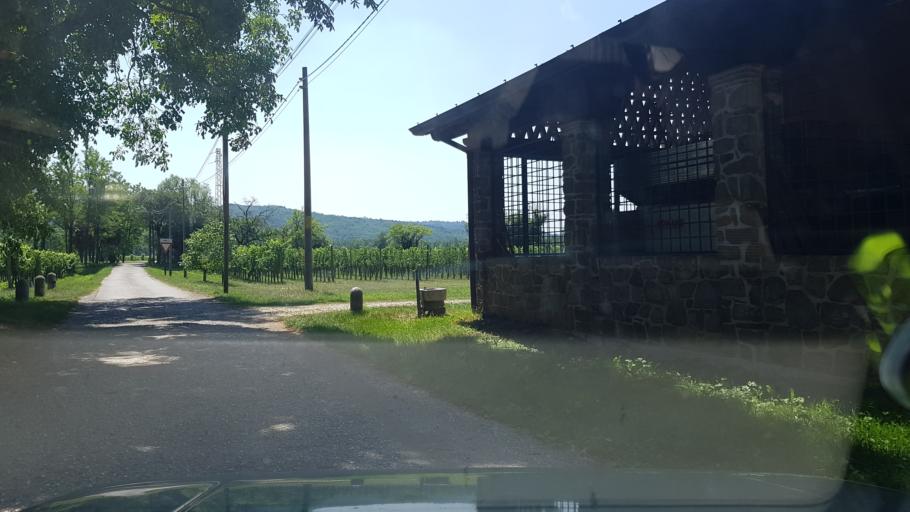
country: IT
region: Friuli Venezia Giulia
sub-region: Provincia di Gorizia
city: Farra d'Isonzo
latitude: 45.9061
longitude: 13.5336
